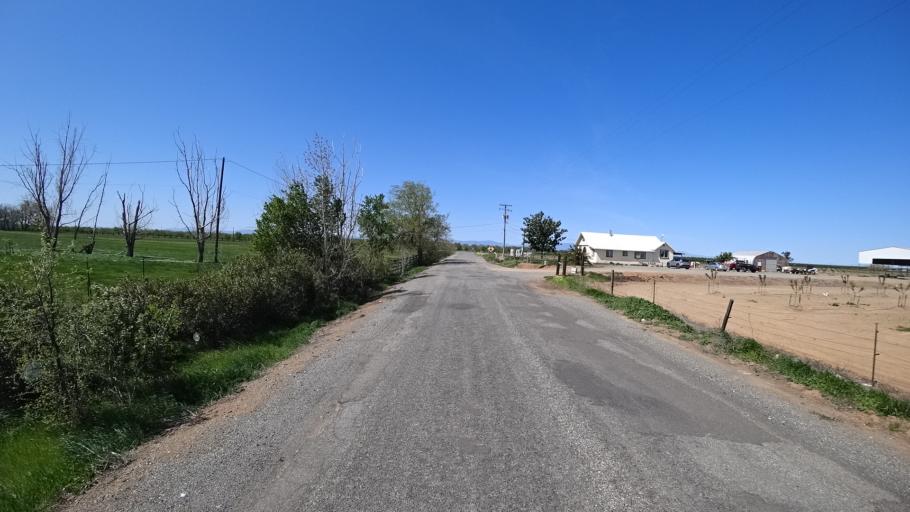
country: US
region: California
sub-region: Glenn County
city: Orland
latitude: 39.7969
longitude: -122.1220
